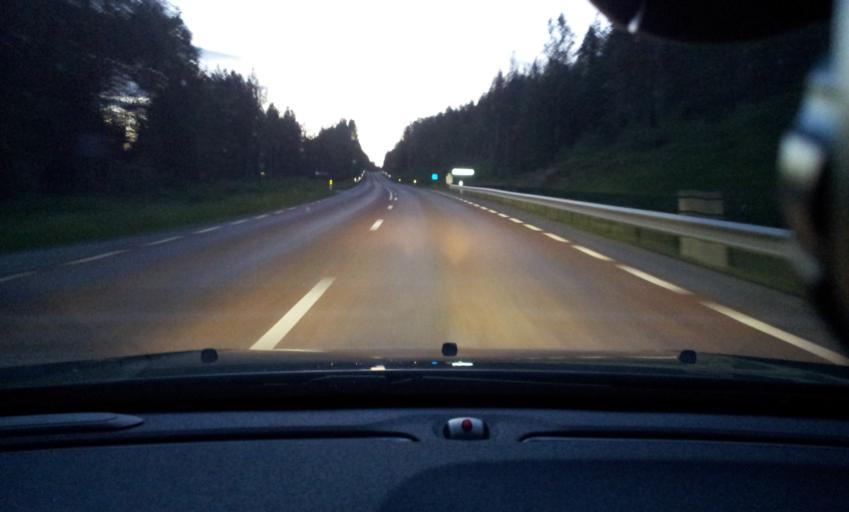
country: SE
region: Jaemtland
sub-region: Bergs Kommun
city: Hoverberg
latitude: 62.8725
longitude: 14.5228
